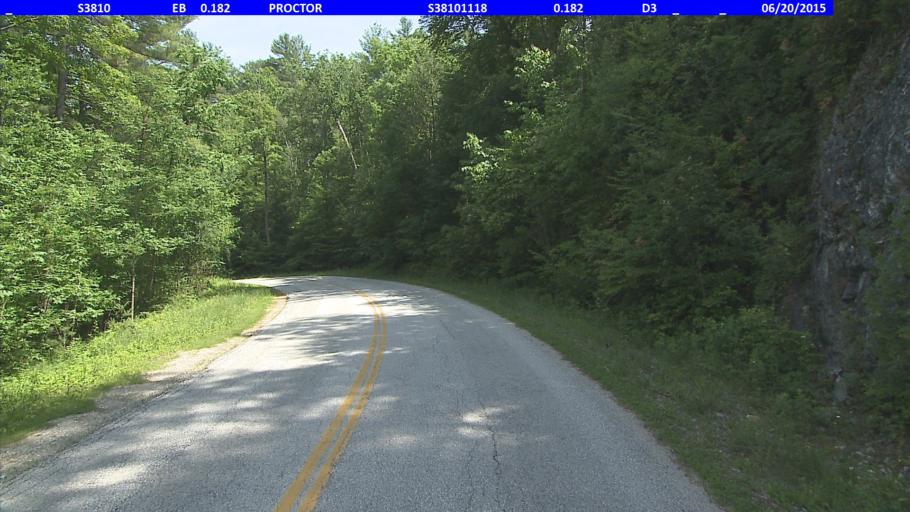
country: US
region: Vermont
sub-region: Rutland County
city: West Rutland
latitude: 43.6669
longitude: -73.0442
